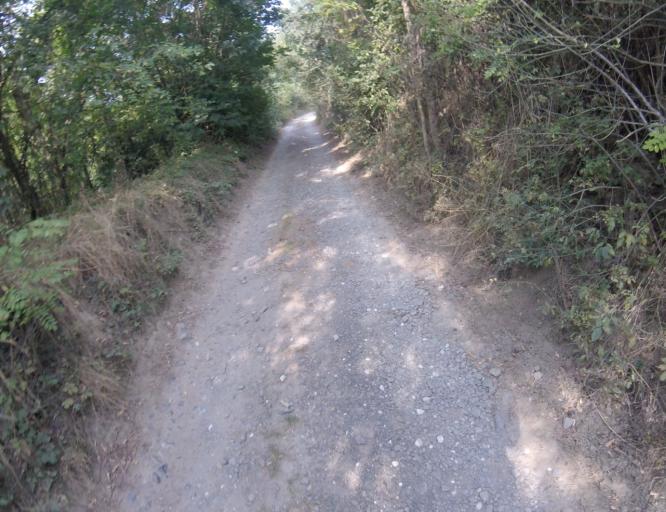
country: HU
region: Pest
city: Veroce
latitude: 47.8264
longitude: 19.0442
